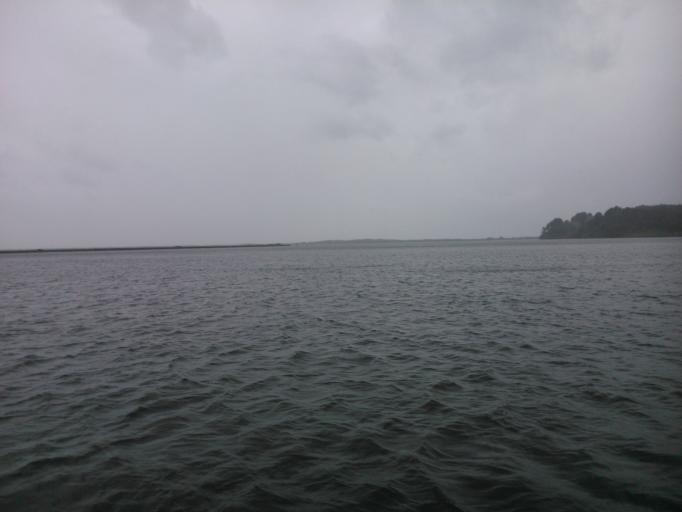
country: CL
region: Araucania
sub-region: Provincia de Cautin
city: Carahue
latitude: -38.7468
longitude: -73.4083
